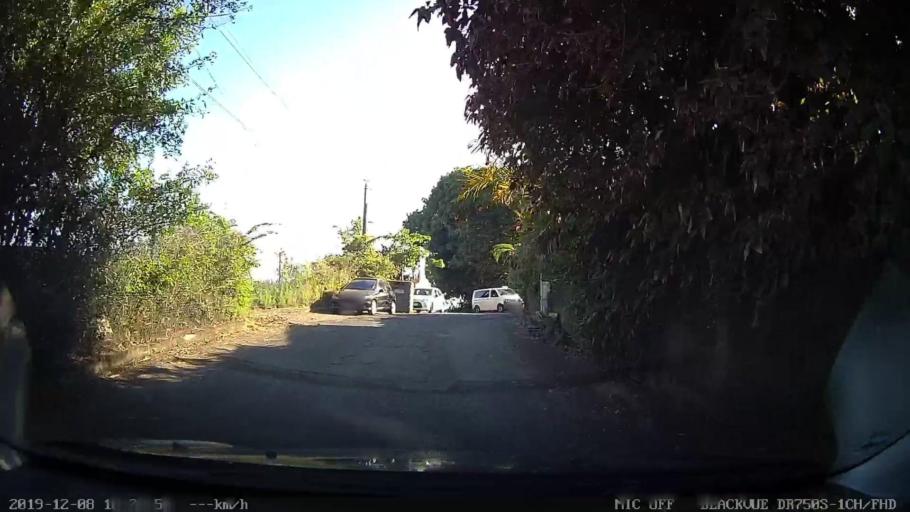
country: RE
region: Reunion
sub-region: Reunion
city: Sainte-Marie
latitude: -20.9255
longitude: 55.5315
